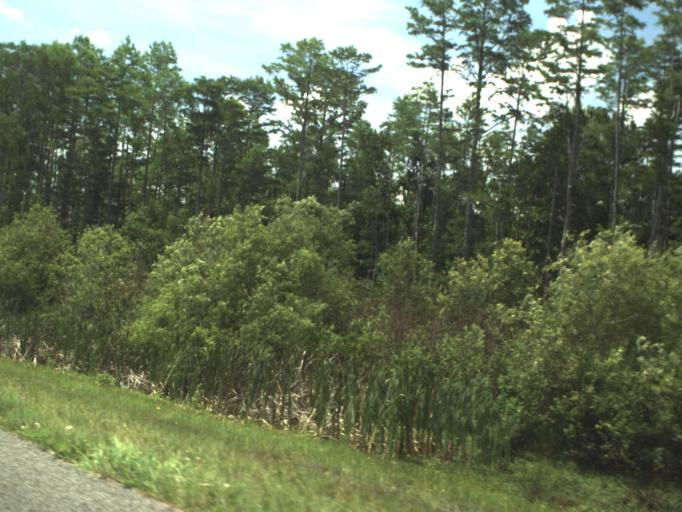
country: US
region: Florida
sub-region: Volusia County
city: Lake Helen
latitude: 29.0301
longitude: -81.1670
